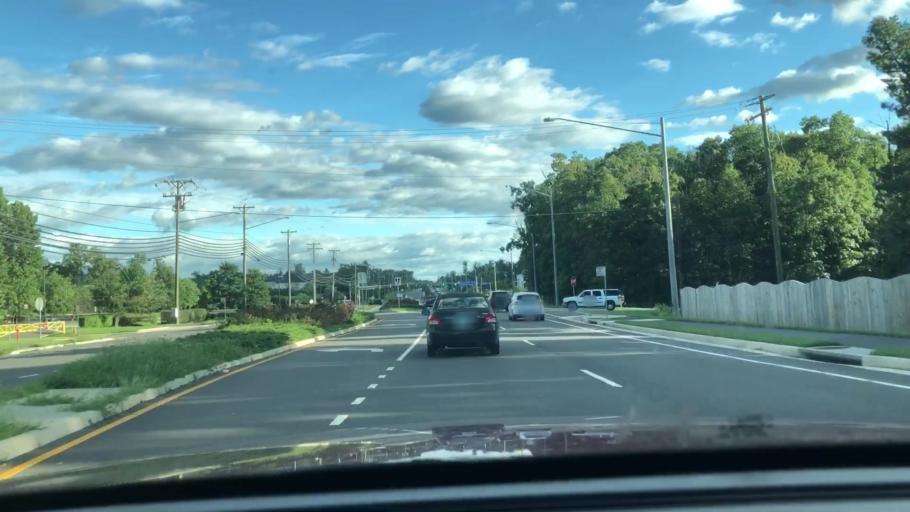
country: US
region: Virginia
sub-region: Fairfax County
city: Greenbriar
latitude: 38.8627
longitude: -77.4061
